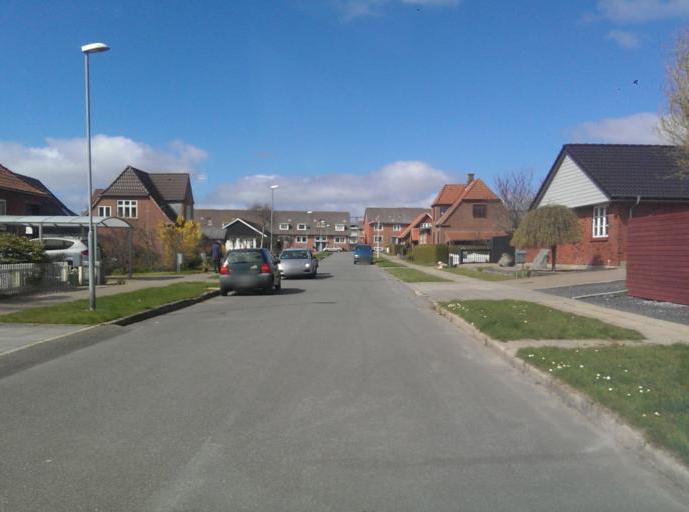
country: DK
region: South Denmark
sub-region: Esbjerg Kommune
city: Esbjerg
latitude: 55.4657
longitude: 8.4665
